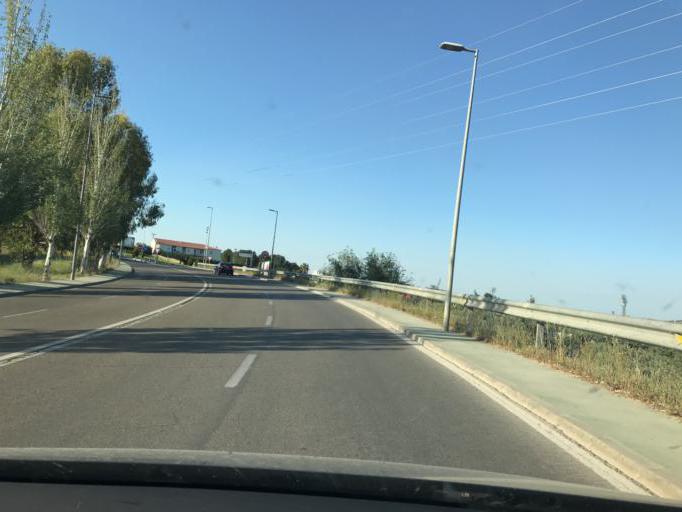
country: ES
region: Andalusia
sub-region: Provincia de Jaen
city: Jaen
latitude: 37.7708
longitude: -3.7716
